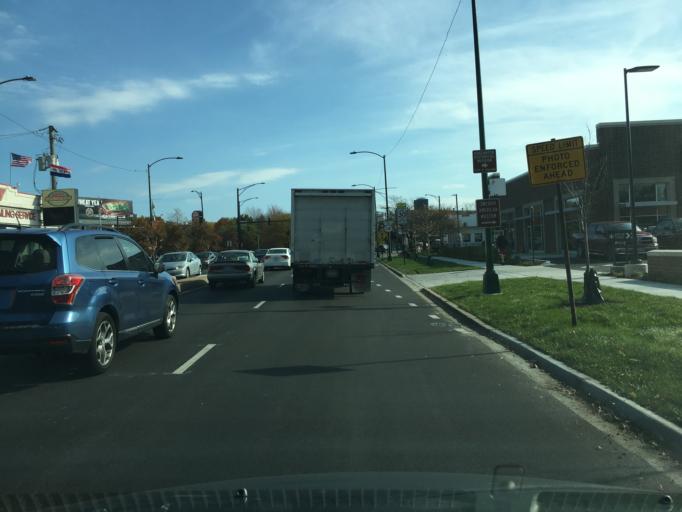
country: US
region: Illinois
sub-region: Cook County
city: Evanston
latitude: 41.9903
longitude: -87.6713
